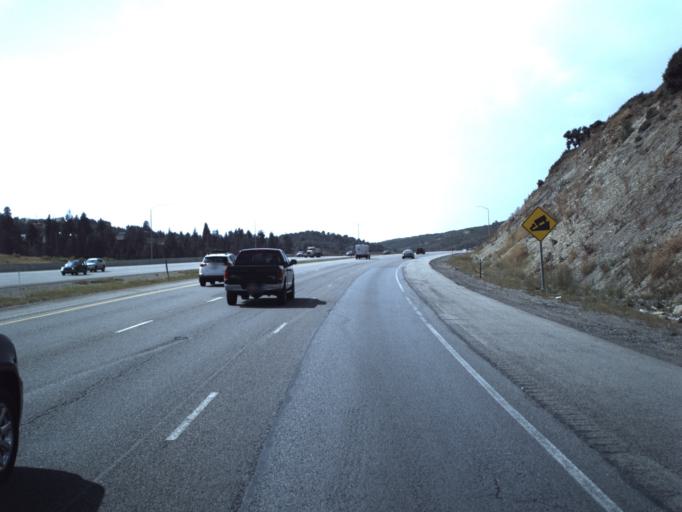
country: US
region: Utah
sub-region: Summit County
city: Summit Park
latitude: 40.7502
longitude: -111.6067
